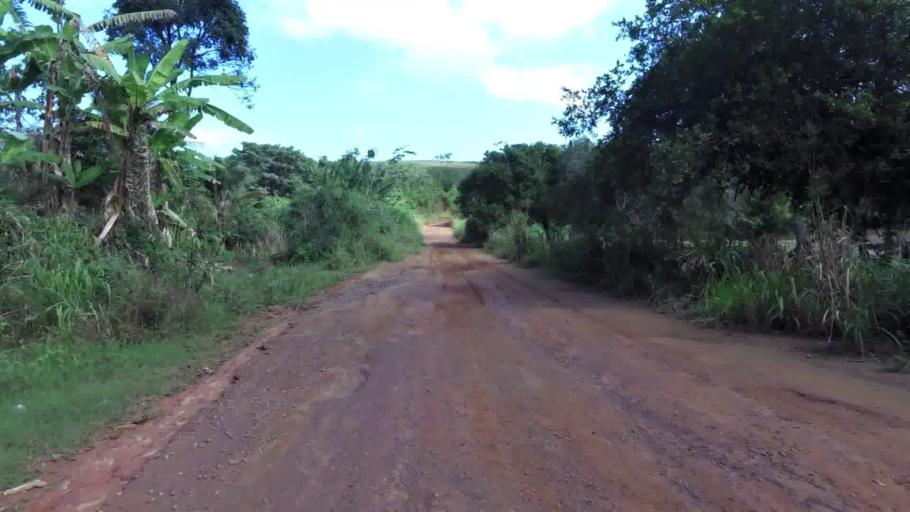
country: BR
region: Espirito Santo
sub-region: Piuma
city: Piuma
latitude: -20.8177
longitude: -40.6765
